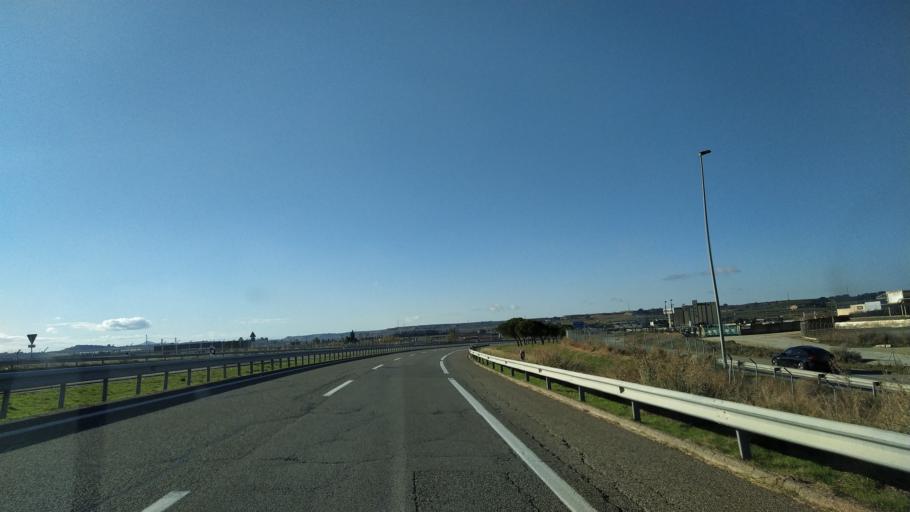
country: ES
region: Catalonia
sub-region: Provincia de Lleida
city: Soses
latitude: 41.5494
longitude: 0.4885
